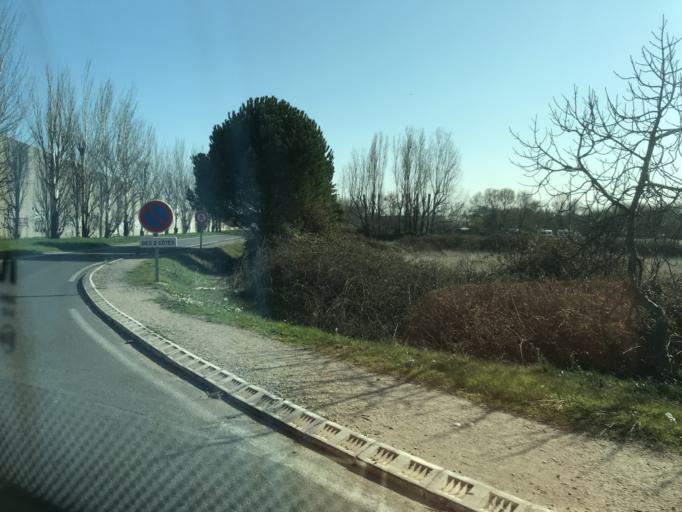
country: FR
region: Languedoc-Roussillon
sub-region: Departement de l'Herault
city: Perols
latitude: 43.5793
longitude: 3.9449
